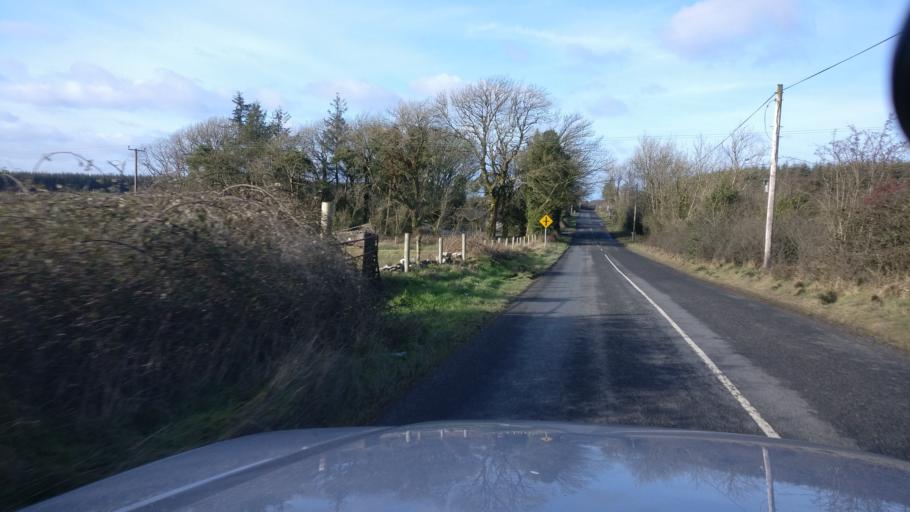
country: IE
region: Leinster
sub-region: Laois
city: Stradbally
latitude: 52.9261
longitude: -7.1947
